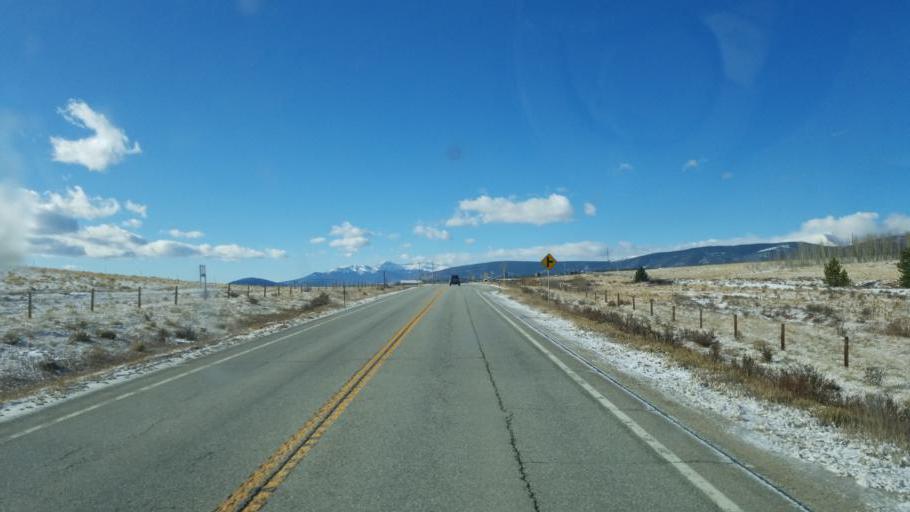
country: US
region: Colorado
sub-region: Park County
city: Fairplay
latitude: 39.2340
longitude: -105.9854
